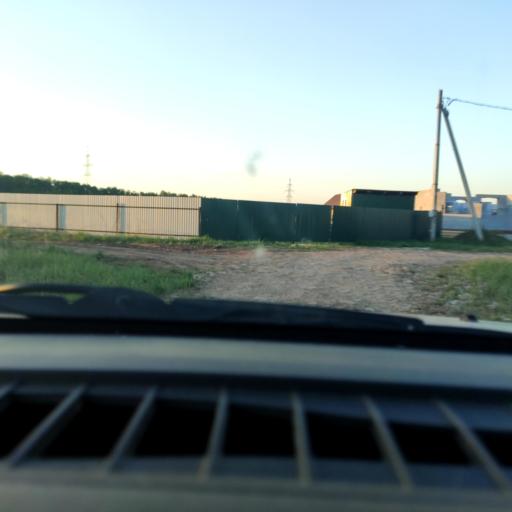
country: RU
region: Perm
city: Froly
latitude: 57.9294
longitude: 56.2886
